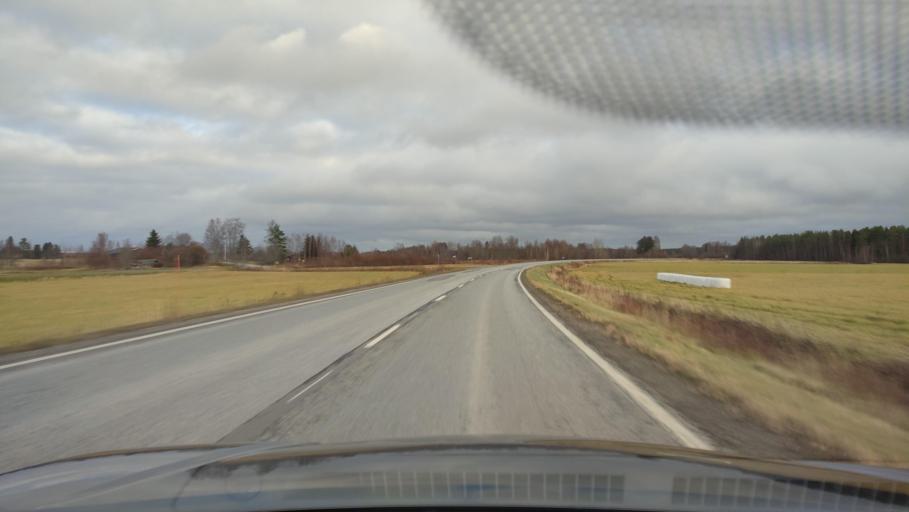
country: FI
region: Southern Ostrobothnia
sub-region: Suupohja
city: Kauhajoki
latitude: 62.3759
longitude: 22.0838
